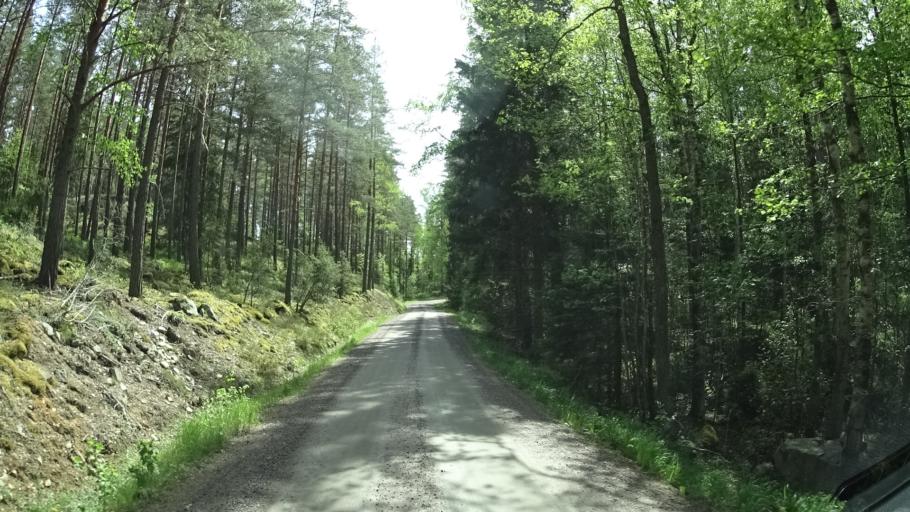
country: SE
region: OEstergoetland
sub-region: Finspangs Kommun
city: Finspang
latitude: 58.7608
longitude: 15.8337
